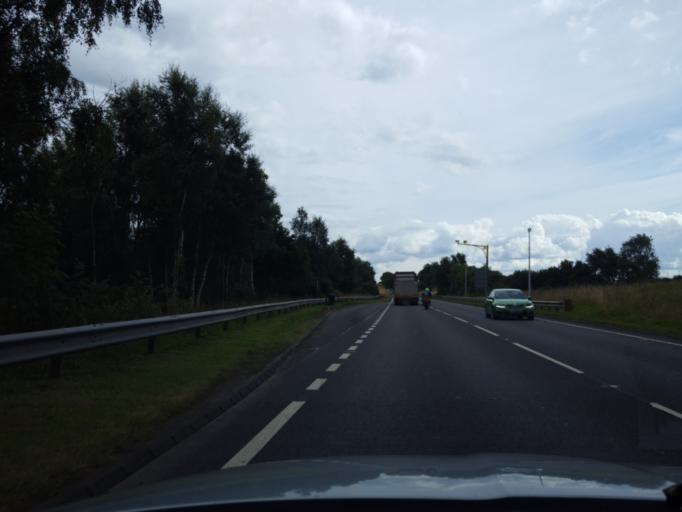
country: GB
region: Scotland
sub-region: Perth and Kinross
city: Luncarty
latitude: 56.4574
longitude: -3.4761
